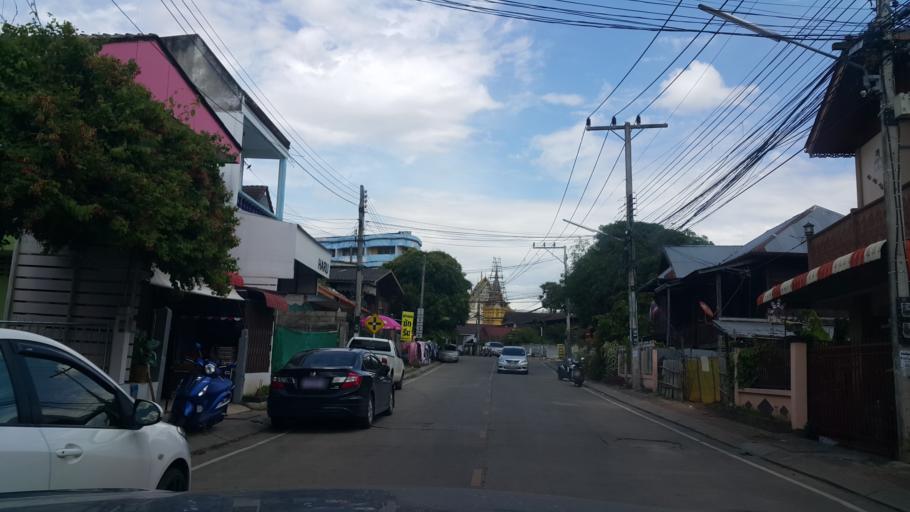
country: TH
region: Phayao
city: Phayao
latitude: 19.1657
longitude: 99.8988
